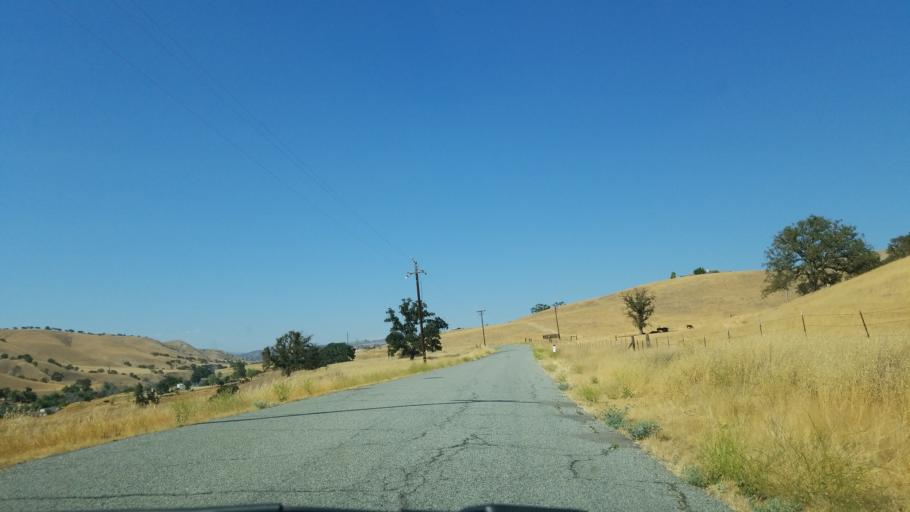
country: US
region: California
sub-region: San Luis Obispo County
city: San Miguel
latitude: 35.7947
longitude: -120.7173
